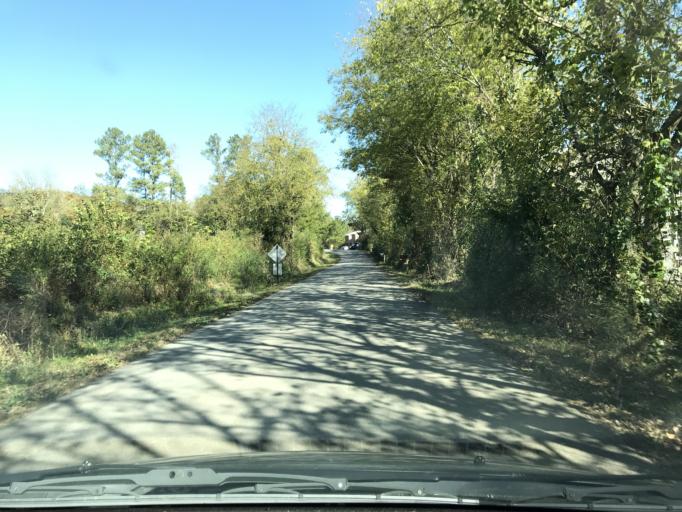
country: US
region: Georgia
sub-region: Dade County
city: Trenton
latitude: 34.9007
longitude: -85.4615
